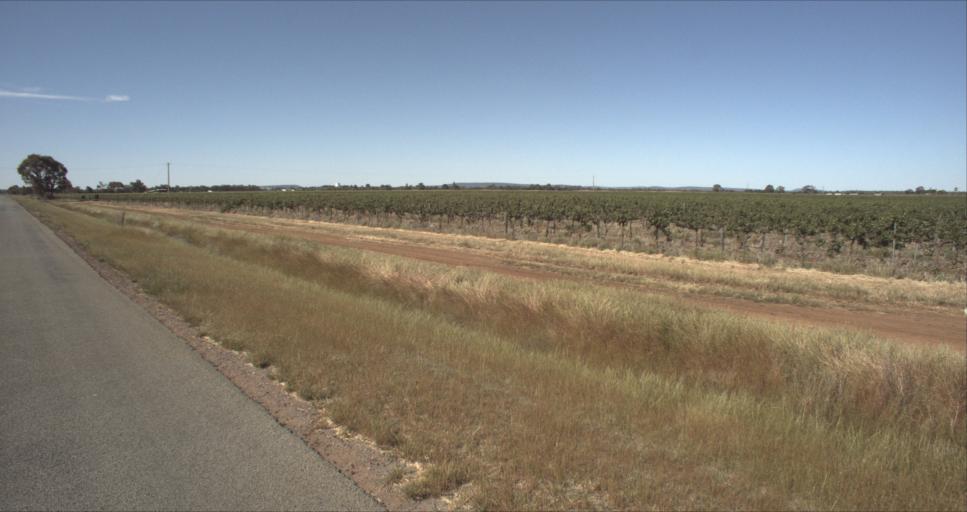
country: AU
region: New South Wales
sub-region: Leeton
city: Leeton
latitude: -34.5800
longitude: 146.3800
